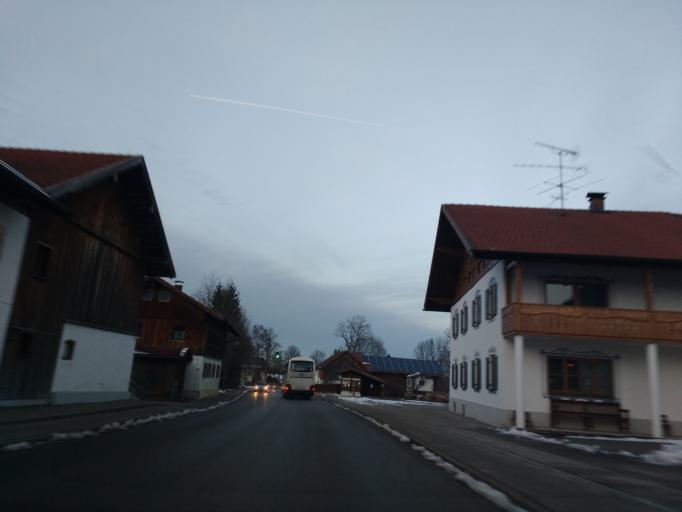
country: DE
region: Bavaria
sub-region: Swabia
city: Halblech
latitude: 47.6301
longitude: 10.8208
